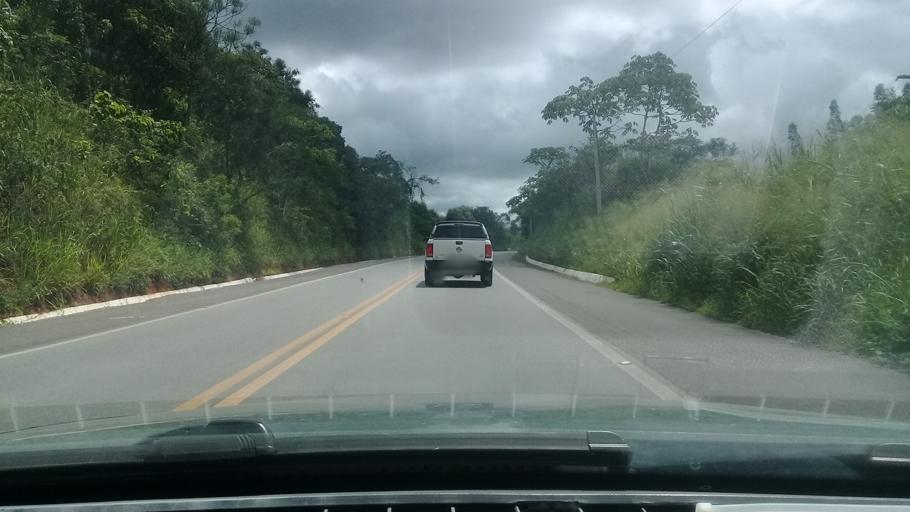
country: BR
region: Pernambuco
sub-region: Nazare Da Mata
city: Nazare da Mata
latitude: -7.7132
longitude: -35.2384
